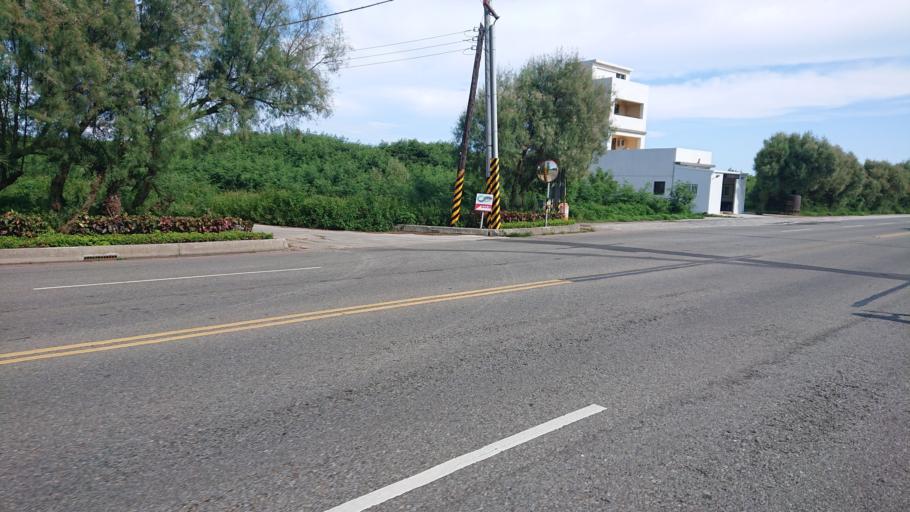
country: TW
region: Taiwan
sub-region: Penghu
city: Ma-kung
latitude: 23.5351
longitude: 119.6028
